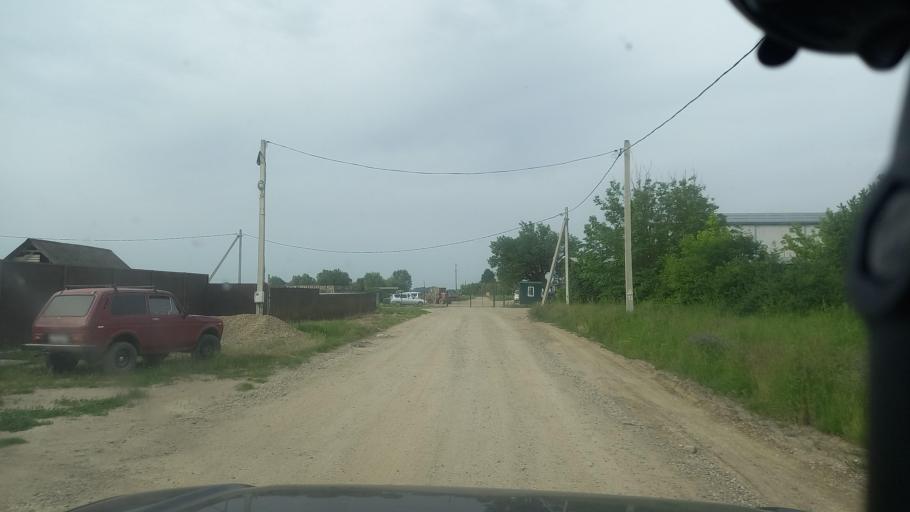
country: RU
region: Krasnodarskiy
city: Saratovskaya
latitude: 44.7554
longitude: 39.2450
